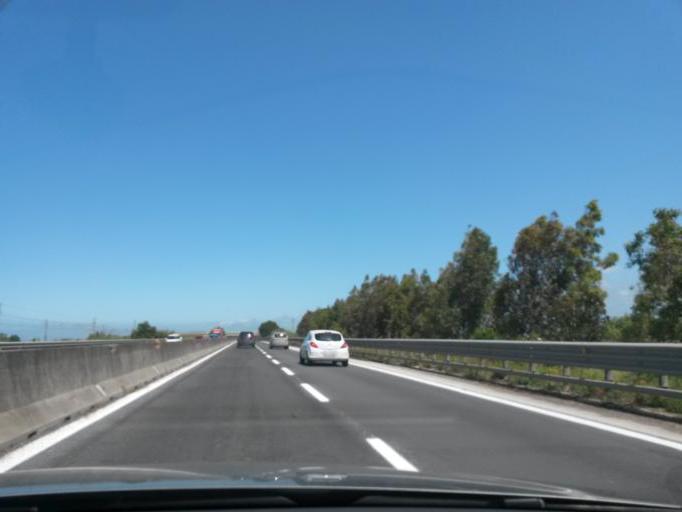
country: IT
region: Tuscany
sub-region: Provincia di Livorno
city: La California
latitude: 43.2542
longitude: 10.5469
